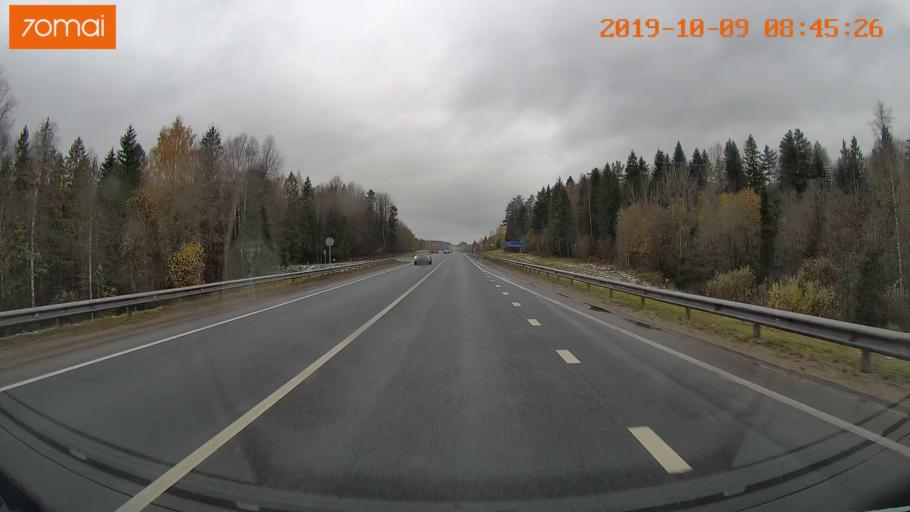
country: RU
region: Vologda
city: Gryazovets
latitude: 59.0480
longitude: 40.0903
